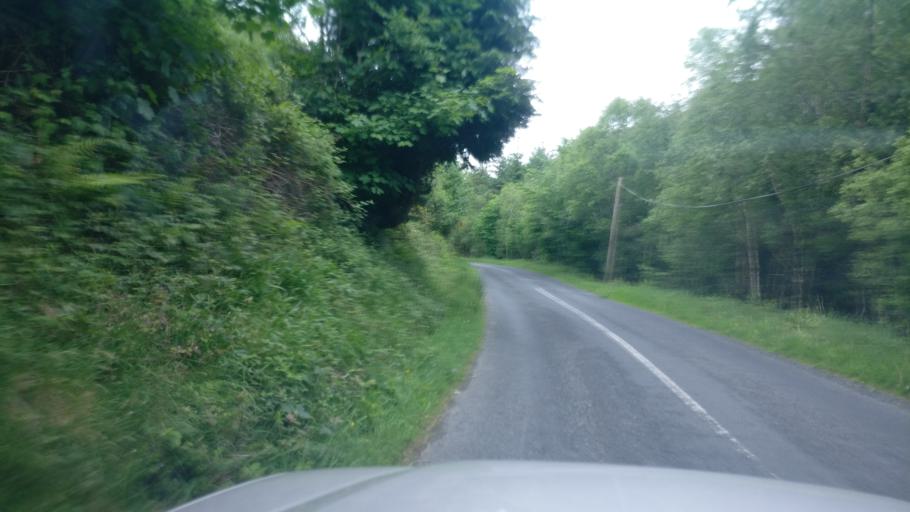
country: IE
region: Connaught
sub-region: County Galway
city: Gort
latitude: 53.0569
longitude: -8.6597
